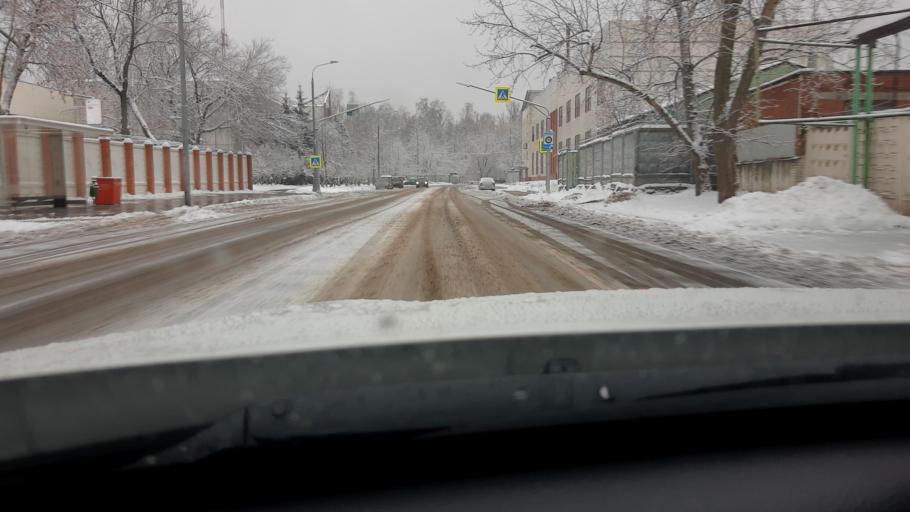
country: RU
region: Moscow
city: Rostokino
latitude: 55.8481
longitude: 37.6866
